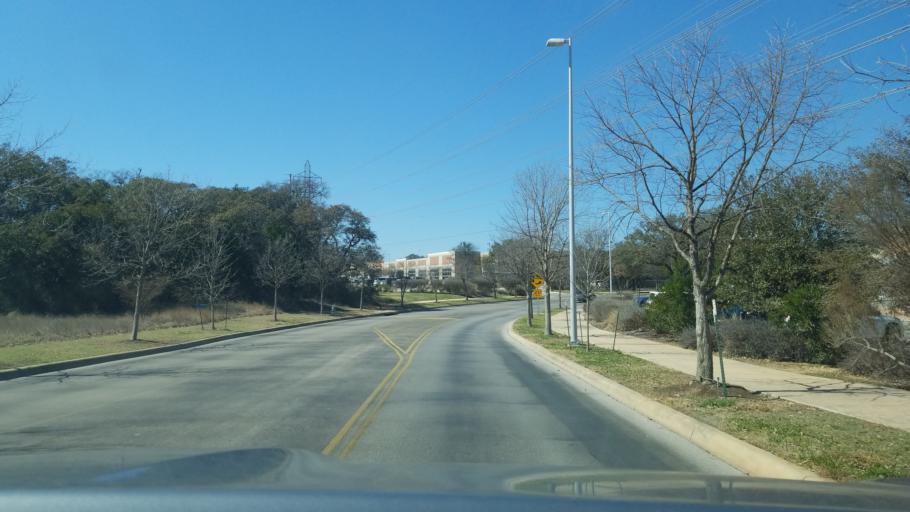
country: US
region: Texas
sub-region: Bexar County
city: Hollywood Park
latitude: 29.6144
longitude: -98.4624
